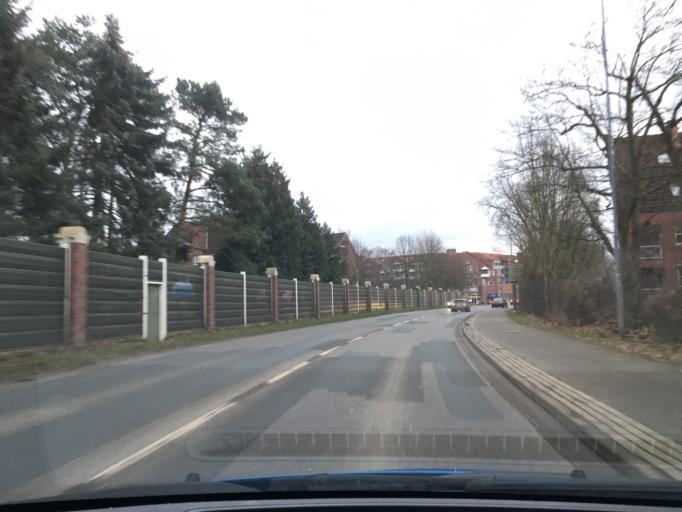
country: DE
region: Lower Saxony
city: Winsen
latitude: 53.3663
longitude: 10.2071
